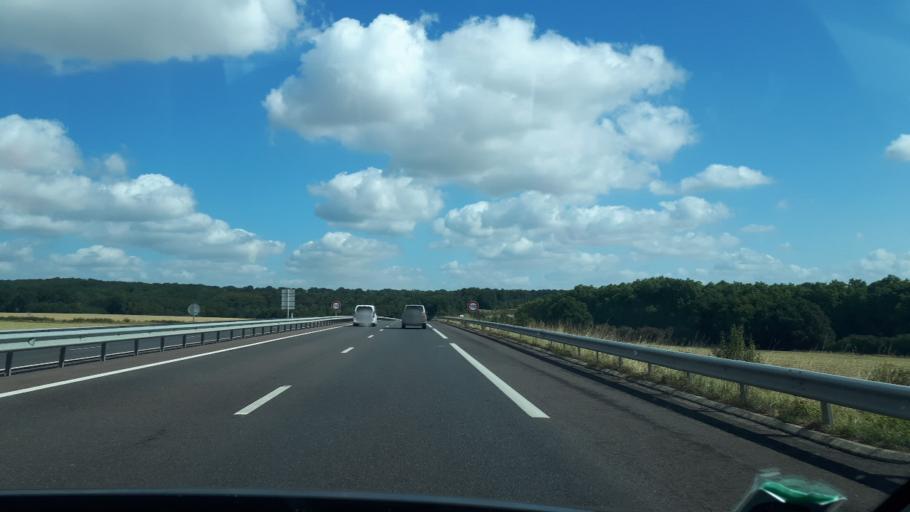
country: FR
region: Centre
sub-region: Departement du Loir-et-Cher
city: Saint-Ouen
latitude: 47.8514
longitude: 1.1062
